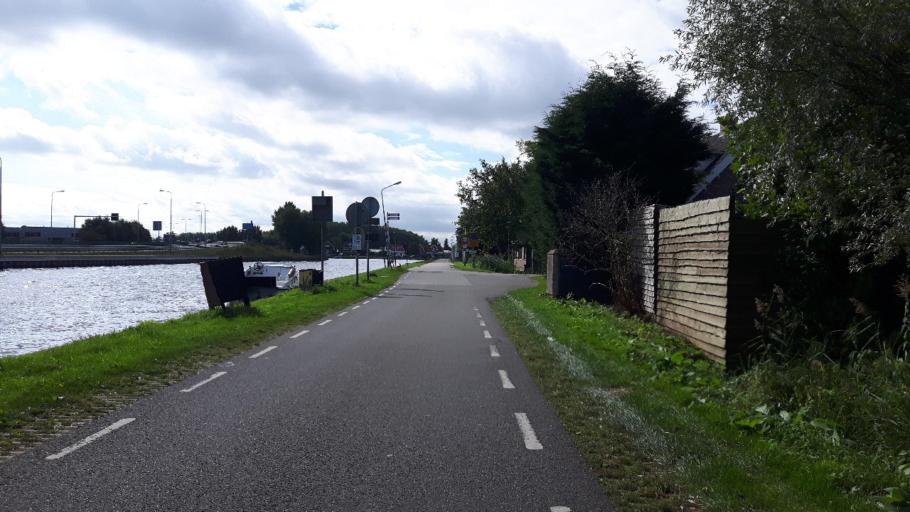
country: NL
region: North Holland
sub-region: Gemeente Landsmeer
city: Landsmeer
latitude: 52.4263
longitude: 4.9502
